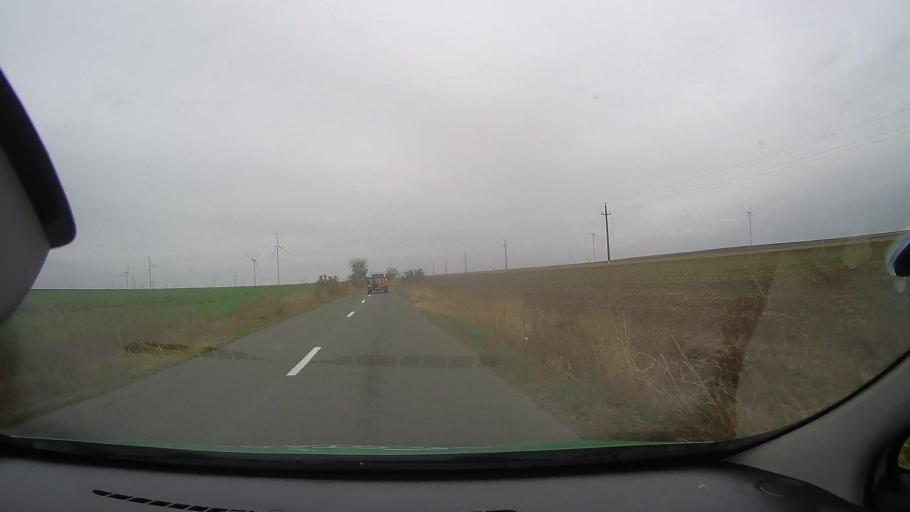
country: RO
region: Constanta
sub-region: Comuna Targusor
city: Targusor
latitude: 44.4731
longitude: 28.3843
